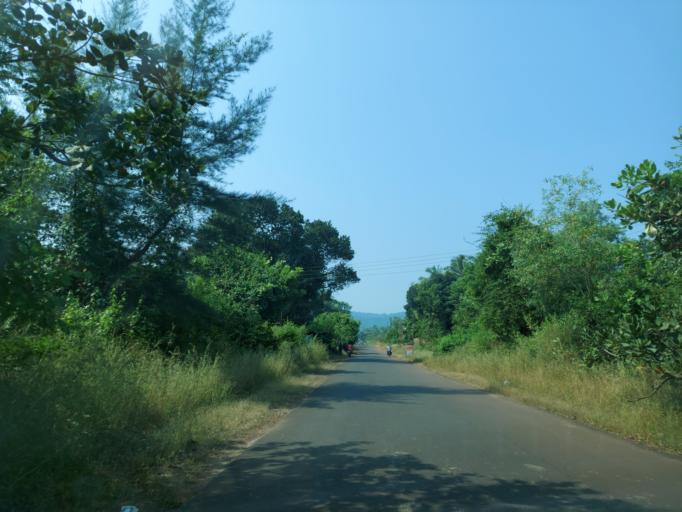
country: IN
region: Maharashtra
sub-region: Sindhudurg
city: Kudal
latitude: 15.9708
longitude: 73.6422
